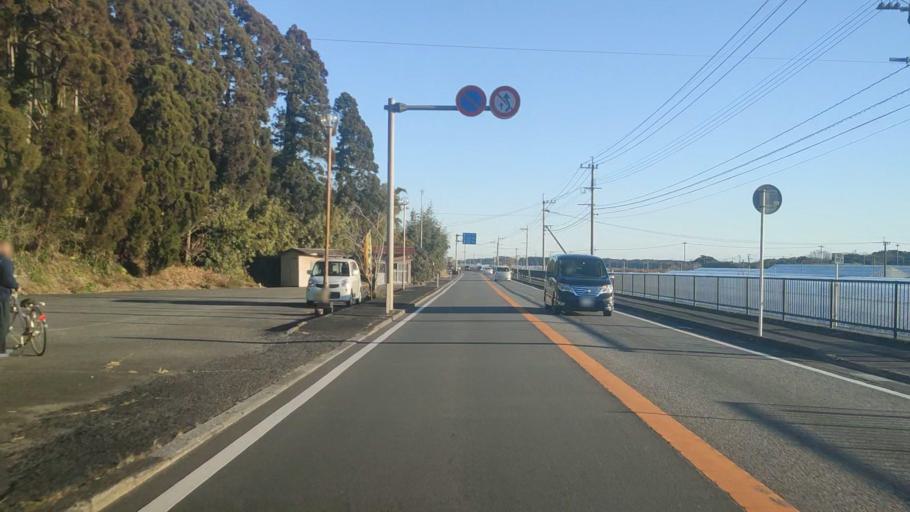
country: JP
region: Miyazaki
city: Takanabe
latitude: 32.0895
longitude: 131.5135
